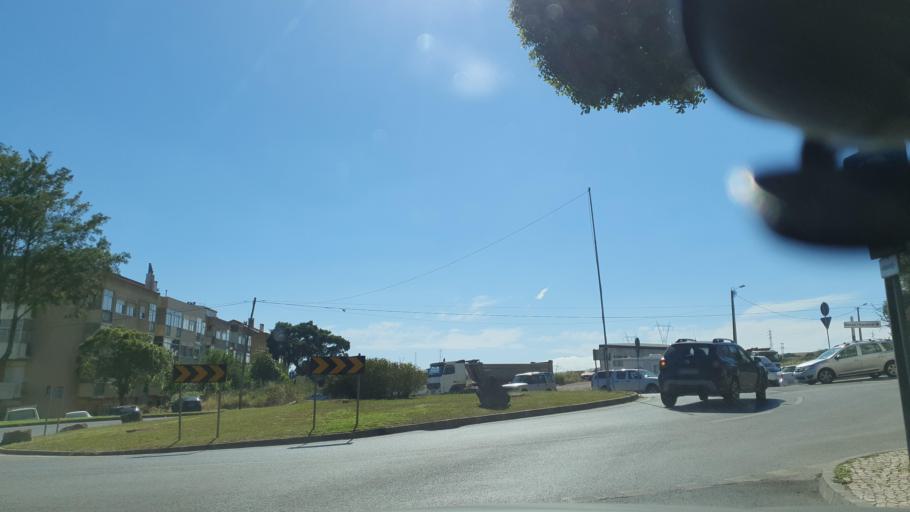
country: PT
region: Lisbon
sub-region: Sintra
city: Cacem
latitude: 38.7580
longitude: -9.2818
